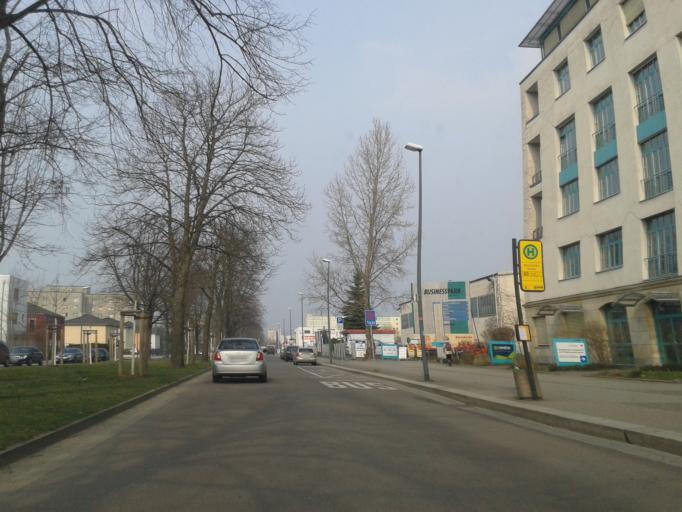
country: DE
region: Saxony
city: Dresden
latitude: 51.0411
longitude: 13.7798
